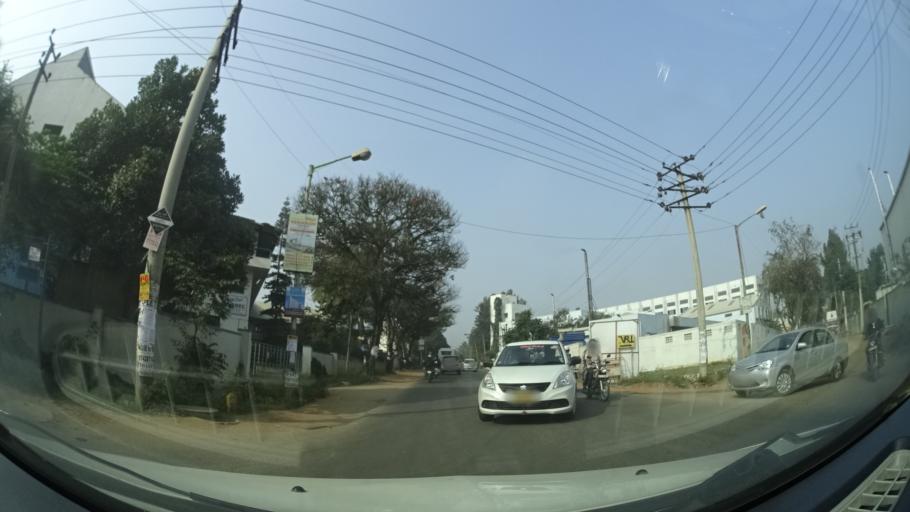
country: IN
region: Karnataka
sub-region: Bangalore Urban
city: Anekal
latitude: 12.8175
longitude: 77.6784
